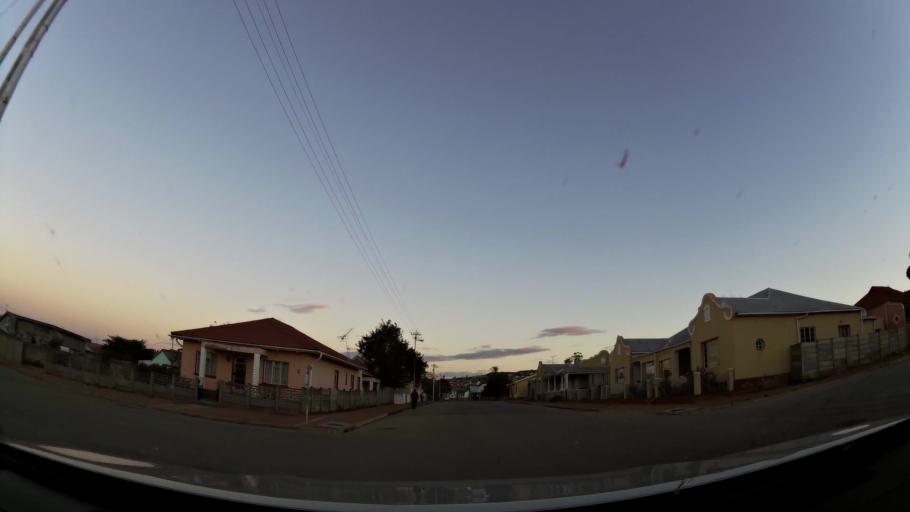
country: ZA
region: Western Cape
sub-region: Eden District Municipality
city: Riversdale
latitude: -34.0940
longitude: 21.2611
